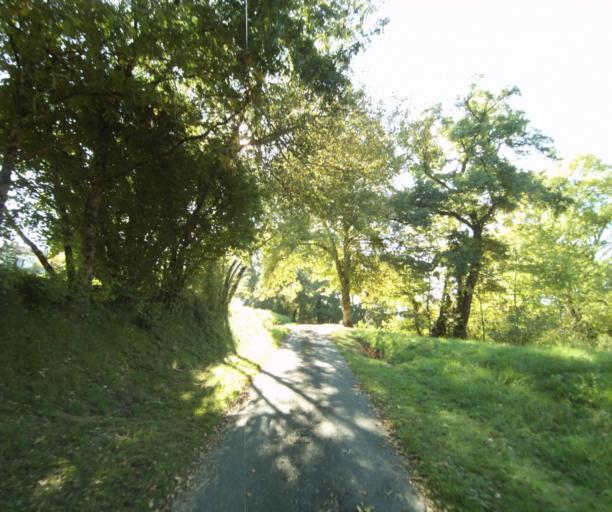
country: FR
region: Midi-Pyrenees
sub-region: Departement du Gers
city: Cazaubon
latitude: 43.9514
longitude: -0.0387
